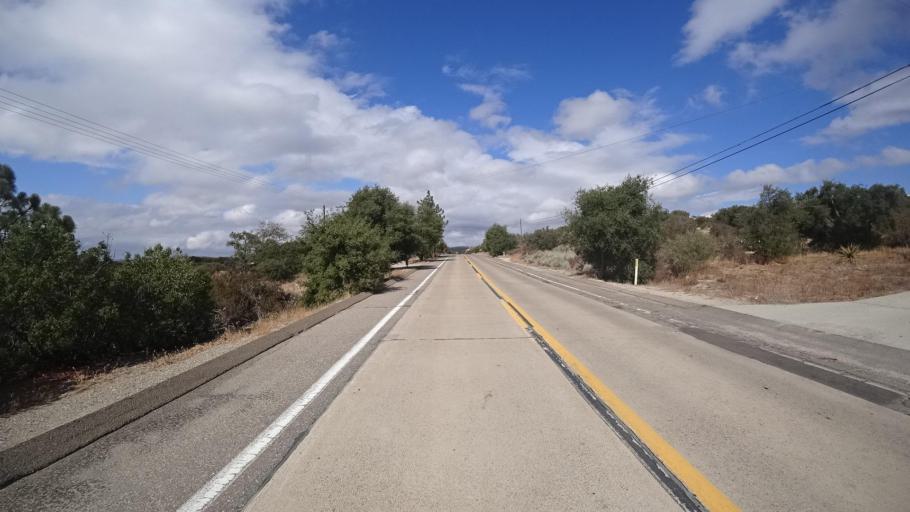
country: US
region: California
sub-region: San Diego County
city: Campo
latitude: 32.6735
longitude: -116.3232
